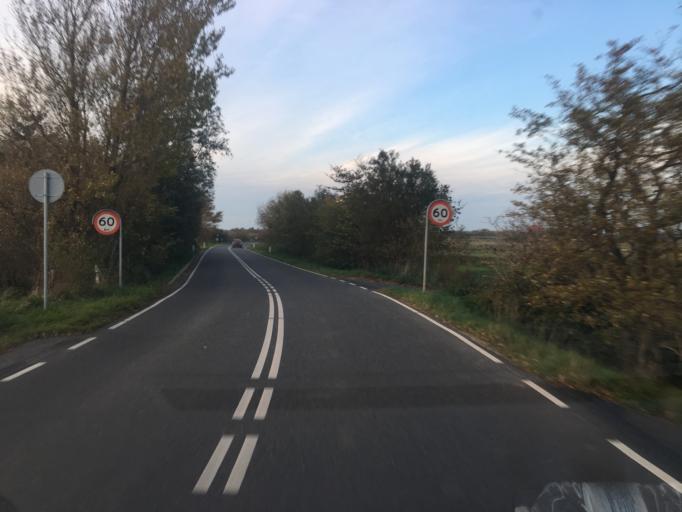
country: DE
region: Schleswig-Holstein
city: Aventoft
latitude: 54.9071
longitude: 8.8328
